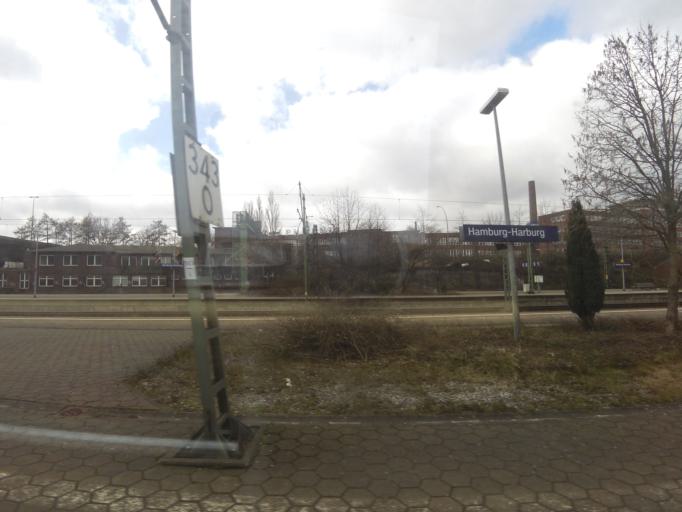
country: DE
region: Hamburg
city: Harburg
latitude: 53.4542
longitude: 9.9927
